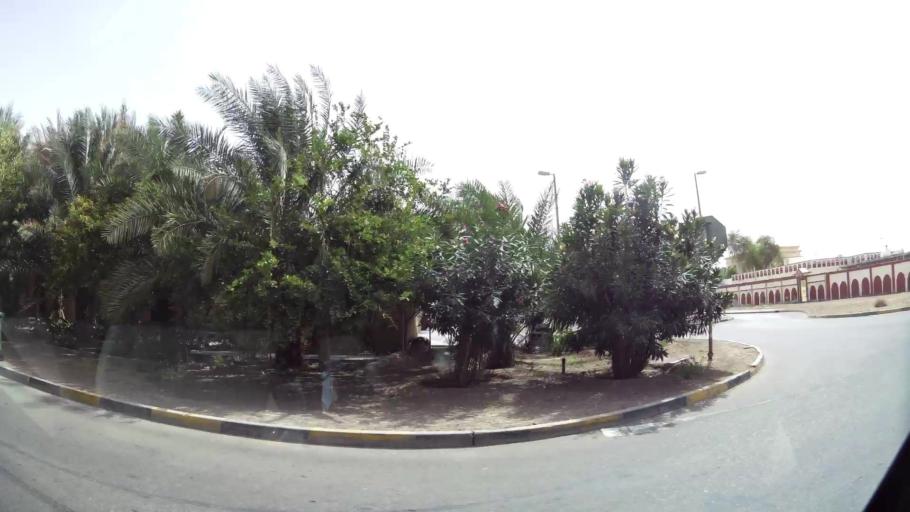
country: AE
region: Abu Dhabi
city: Al Ain
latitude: 24.1923
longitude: 55.6276
